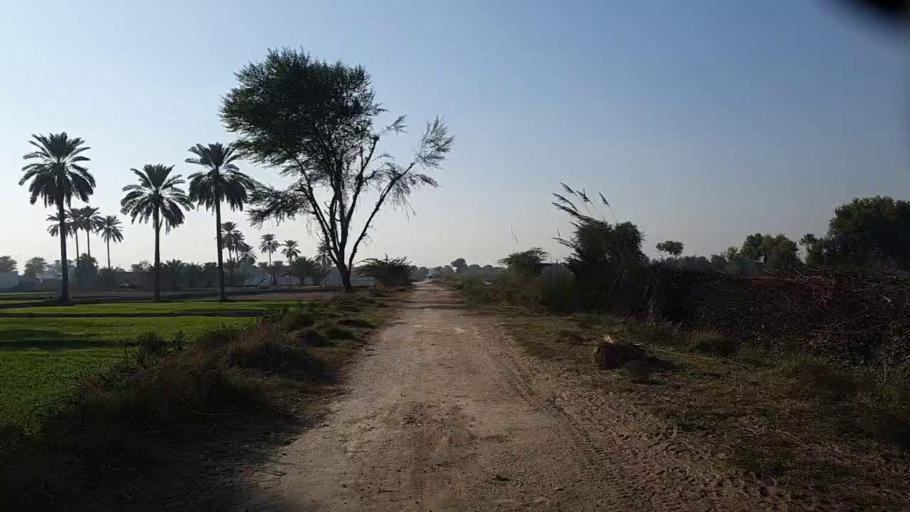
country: PK
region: Sindh
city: Ranipur
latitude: 27.2532
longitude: 68.5384
